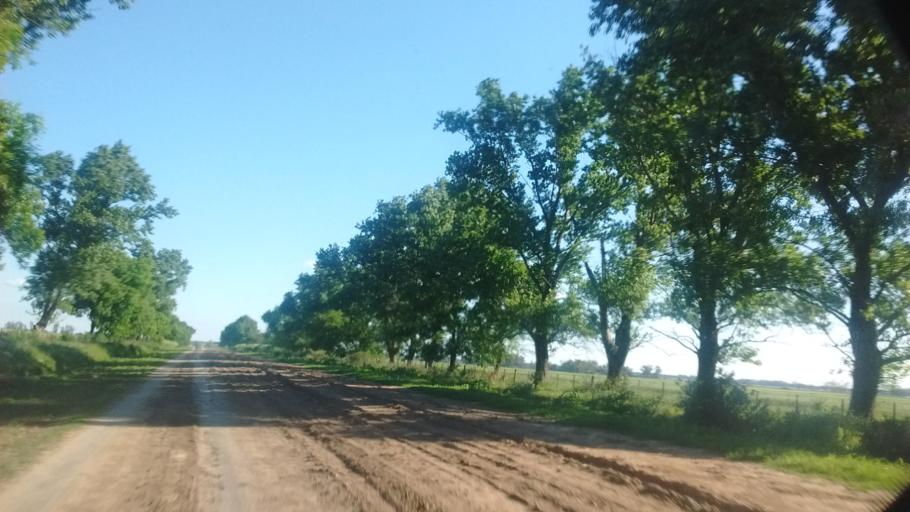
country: AR
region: Santa Fe
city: Funes
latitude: -32.8744
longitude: -60.7985
